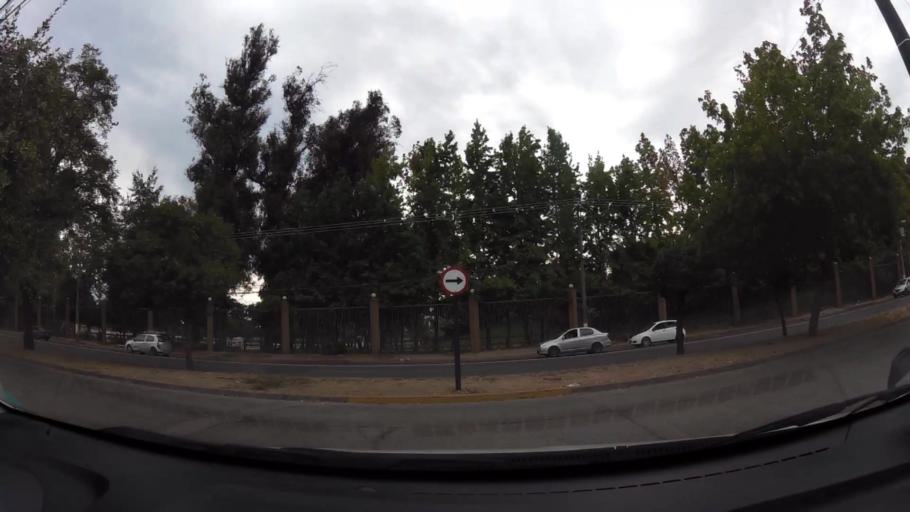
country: CL
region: O'Higgins
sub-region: Provincia de Cachapoal
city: Rancagua
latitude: -34.1575
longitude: -70.7437
